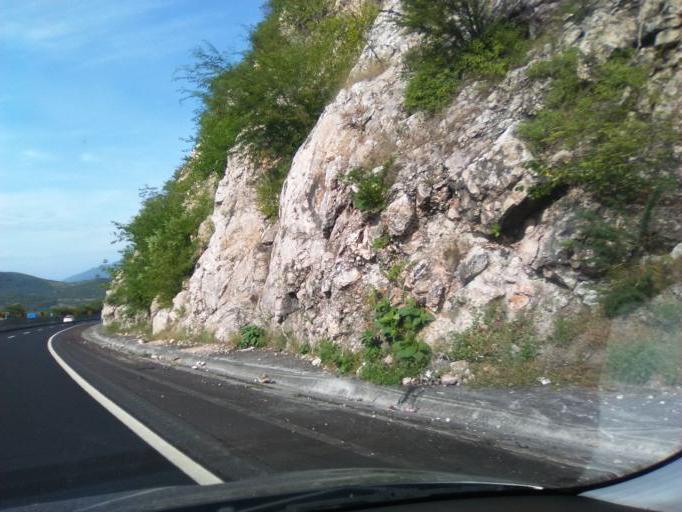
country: MX
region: Morelos
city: Tilzapotla
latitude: 18.4307
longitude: -99.1783
